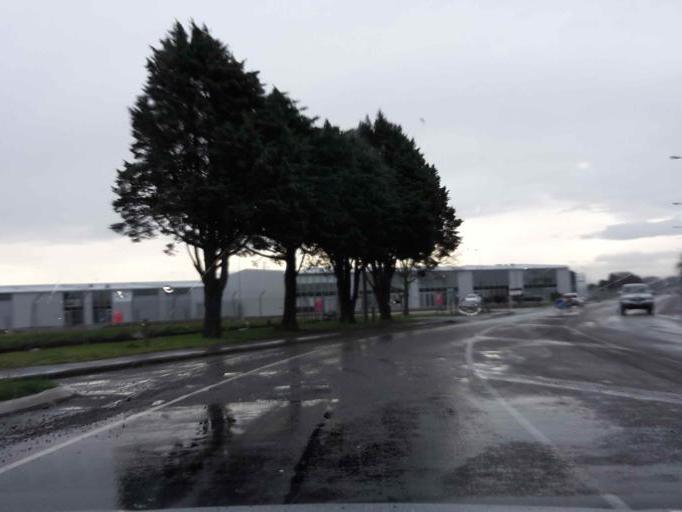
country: NZ
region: Canterbury
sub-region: Selwyn District
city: Prebbleton
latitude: -43.5391
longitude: 172.5494
